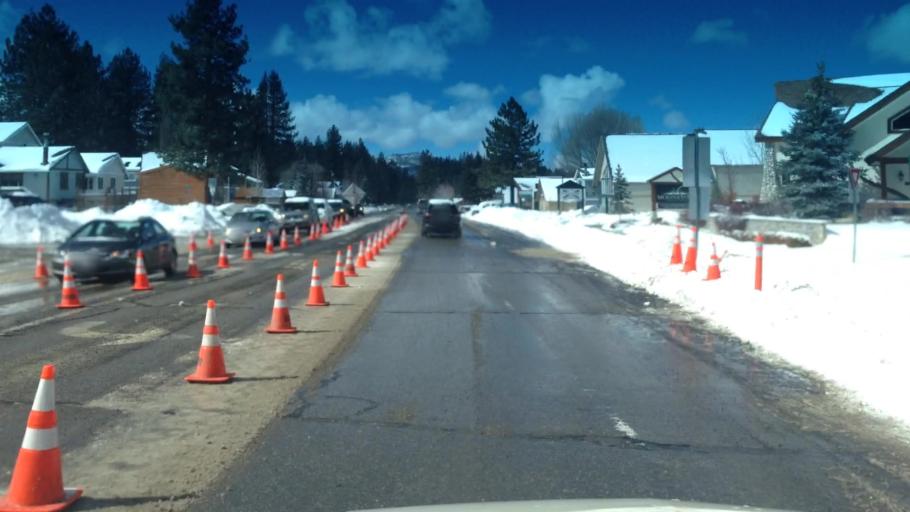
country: US
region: California
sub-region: San Bernardino County
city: Big Bear City
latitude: 34.2397
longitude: -116.8695
